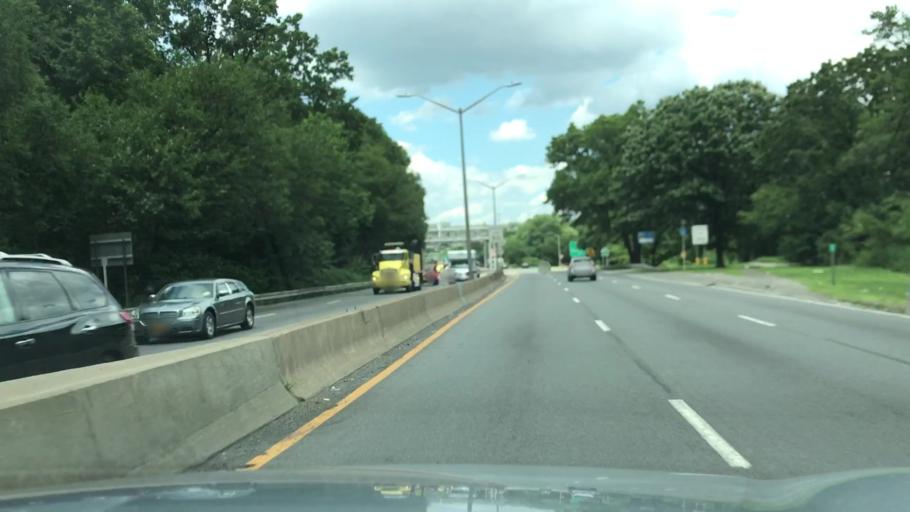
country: US
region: New York
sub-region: Bronx
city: The Bronx
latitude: 40.8447
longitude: -73.8716
